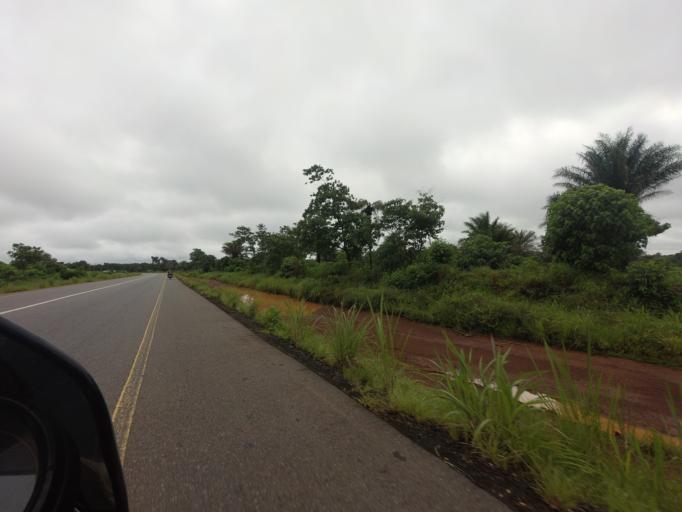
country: SL
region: Northern Province
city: Kambia
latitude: 9.0874
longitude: -12.9097
